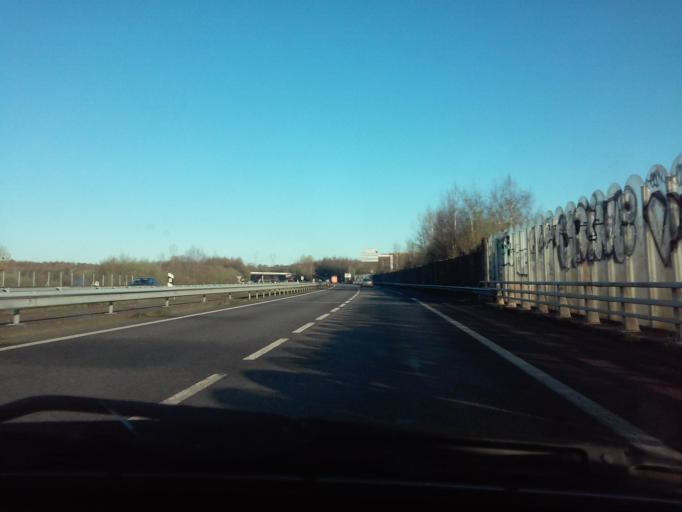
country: FR
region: Brittany
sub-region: Departement d'Ille-et-Vilaine
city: Fouillard
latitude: 48.1365
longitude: -1.5765
